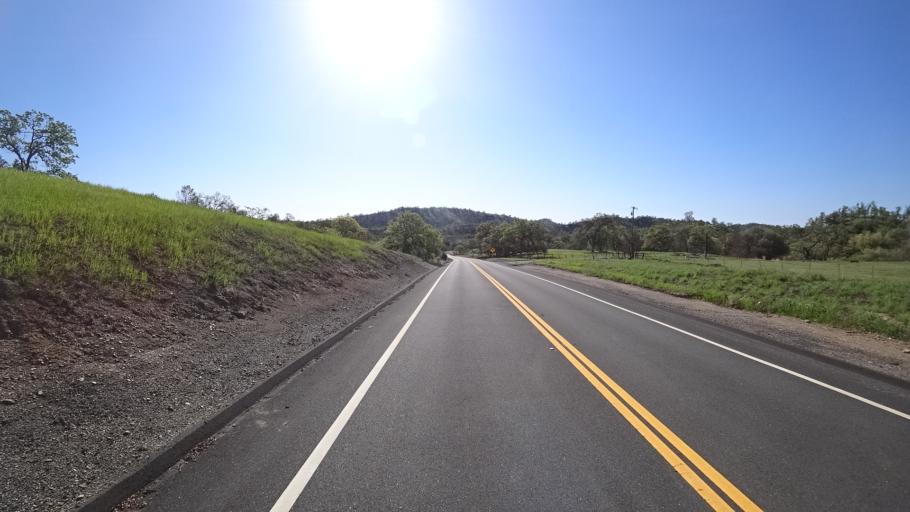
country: US
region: California
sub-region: Glenn County
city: Orland
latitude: 39.6560
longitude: -122.5900
